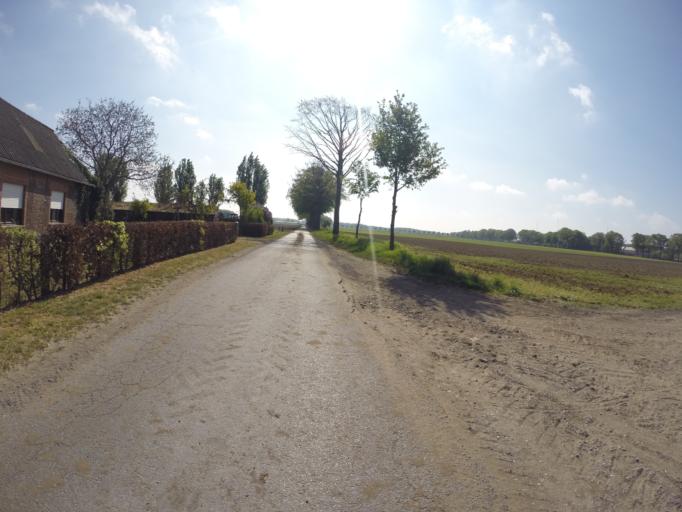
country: BE
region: Flanders
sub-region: Provincie West-Vlaanderen
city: Beernem
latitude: 51.0944
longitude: 3.3423
